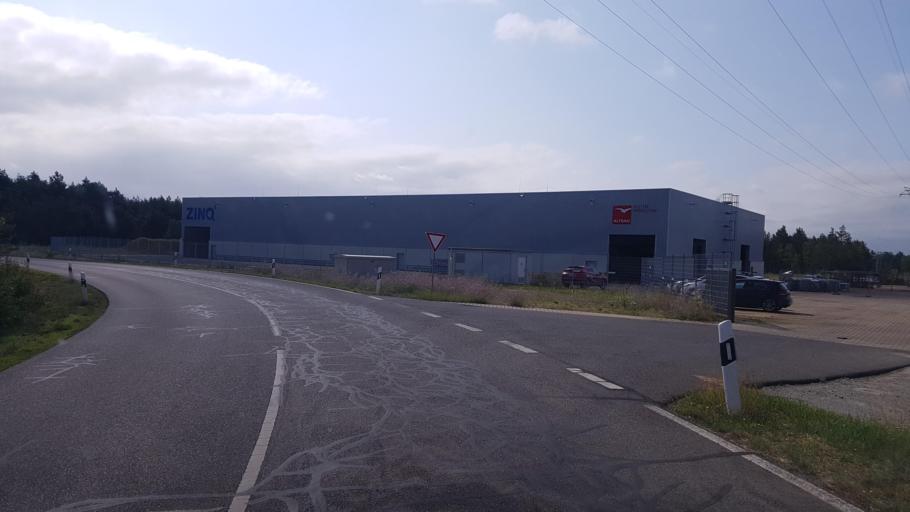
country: DE
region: Brandenburg
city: Grossraschen
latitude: 51.5940
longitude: 14.0259
